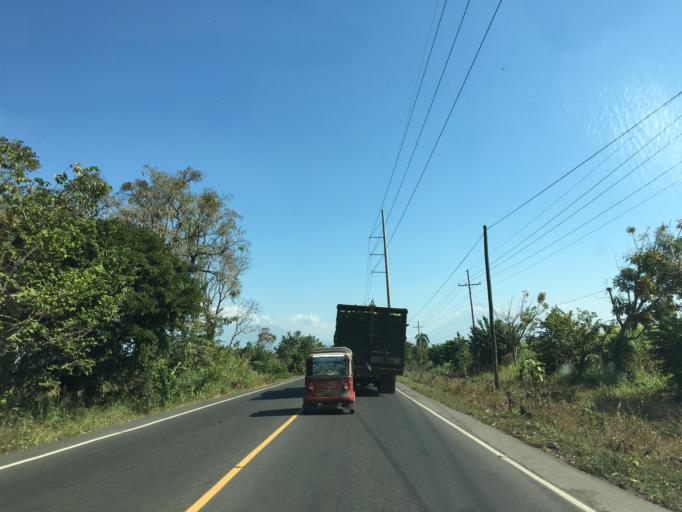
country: GT
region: Escuintla
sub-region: Municipio de La Democracia
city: La Democracia
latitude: 14.2126
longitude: -90.9560
